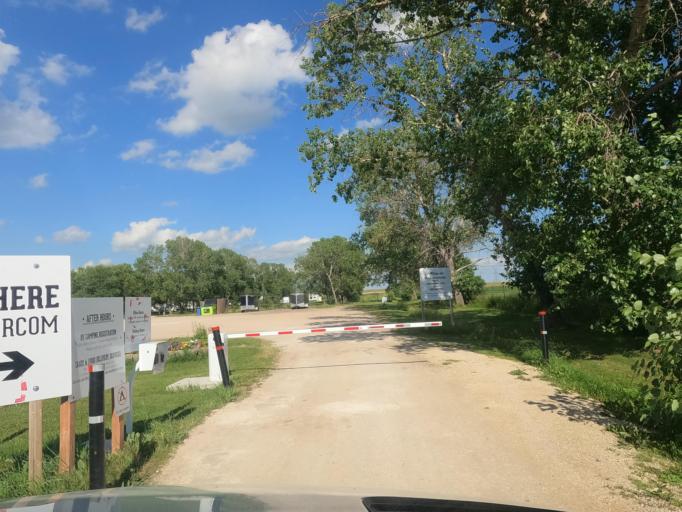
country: CA
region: Manitoba
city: Winnipeg
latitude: 49.8267
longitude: -96.9784
